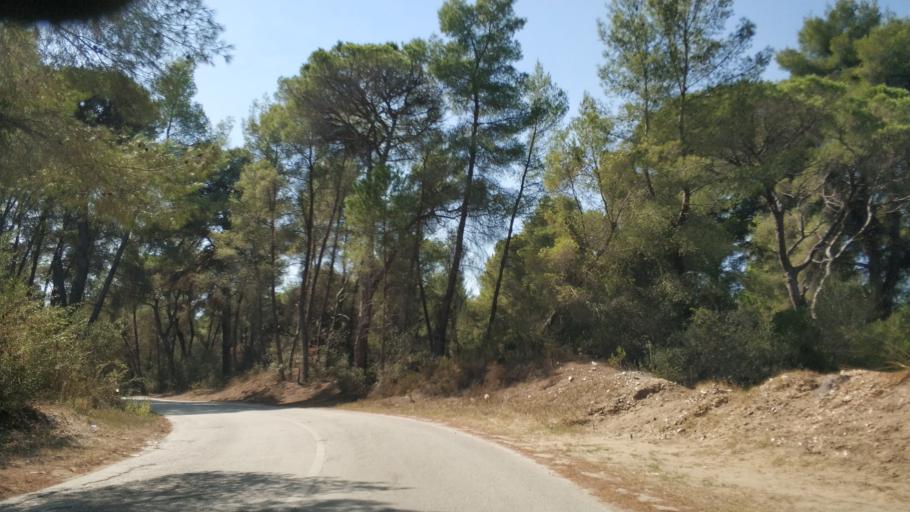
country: AL
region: Fier
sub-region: Rrethi i Lushnjes
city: Divjake
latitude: 40.9868
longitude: 19.4838
